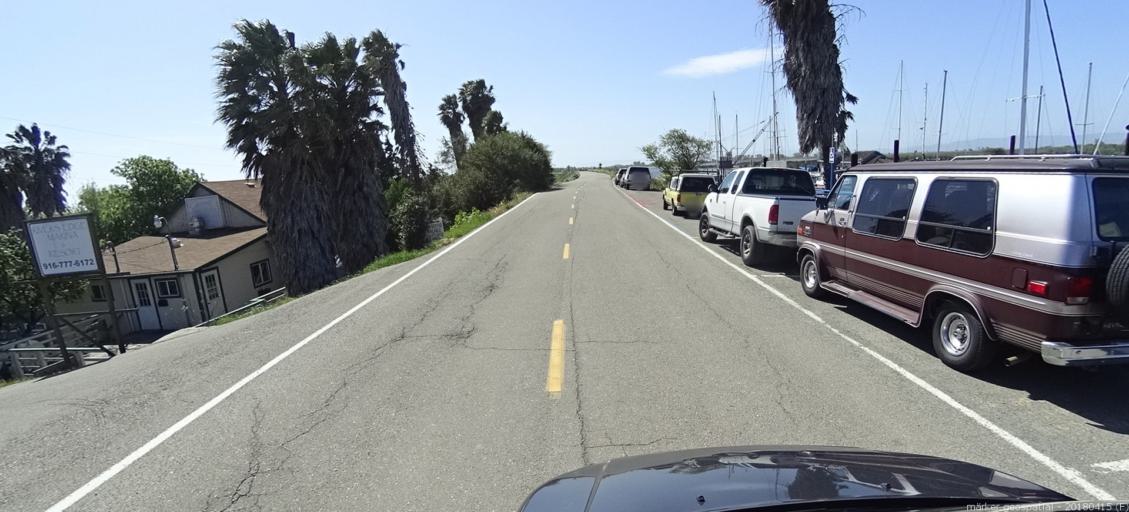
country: US
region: California
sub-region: Solano County
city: Rio Vista
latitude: 38.1115
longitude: -121.6139
